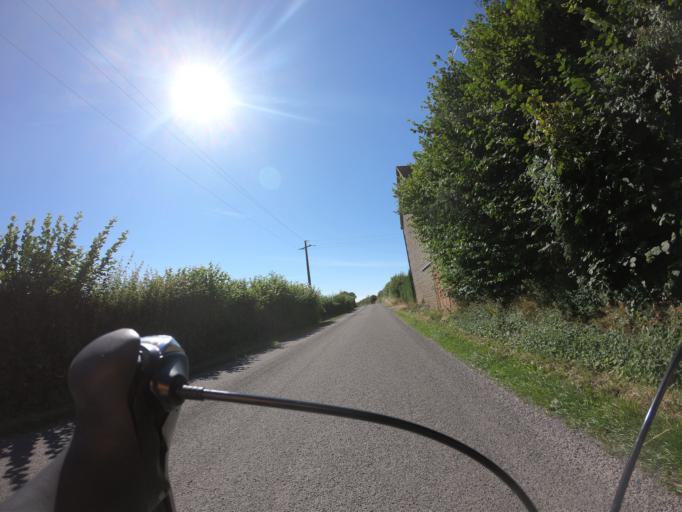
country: FR
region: Lower Normandy
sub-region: Departement de l'Orne
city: Saint-Denis-sur-Sarthon
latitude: 48.5440
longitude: -0.1046
